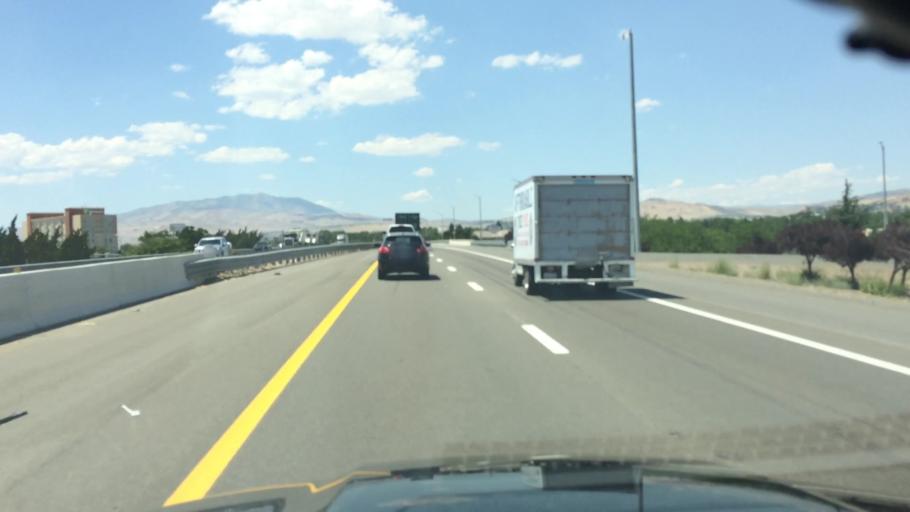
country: US
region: Nevada
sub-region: Washoe County
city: Sparks
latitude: 39.5325
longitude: -119.7367
